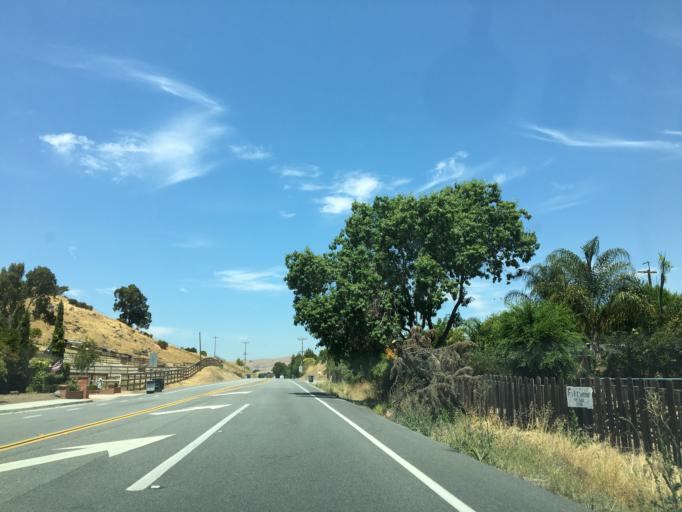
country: US
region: California
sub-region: Santa Clara County
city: Morgan Hill
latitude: 37.1423
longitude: -121.6686
